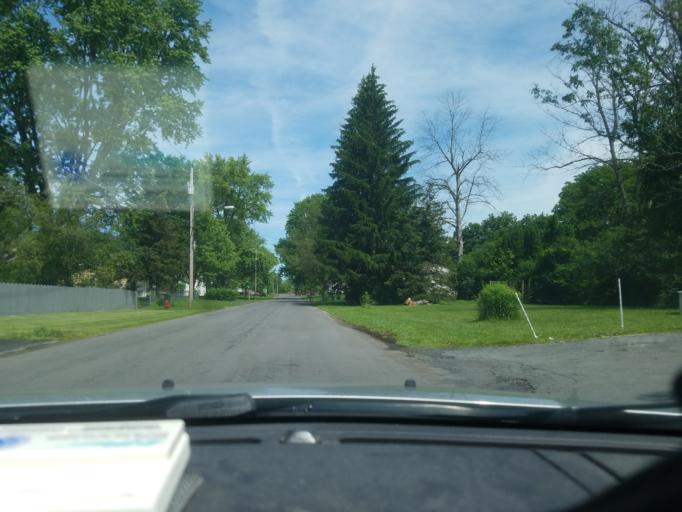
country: US
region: New York
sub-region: Onondaga County
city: East Syracuse
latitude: 43.0829
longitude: -76.0679
